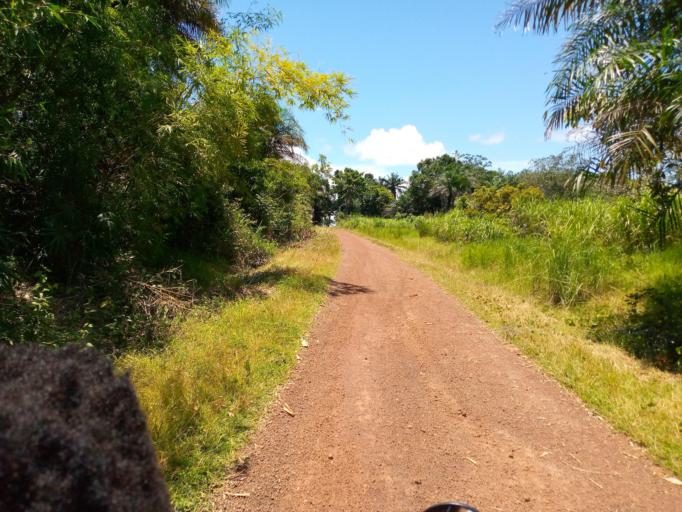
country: SL
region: Northern Province
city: Binkolo
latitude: 9.1097
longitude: -12.1379
